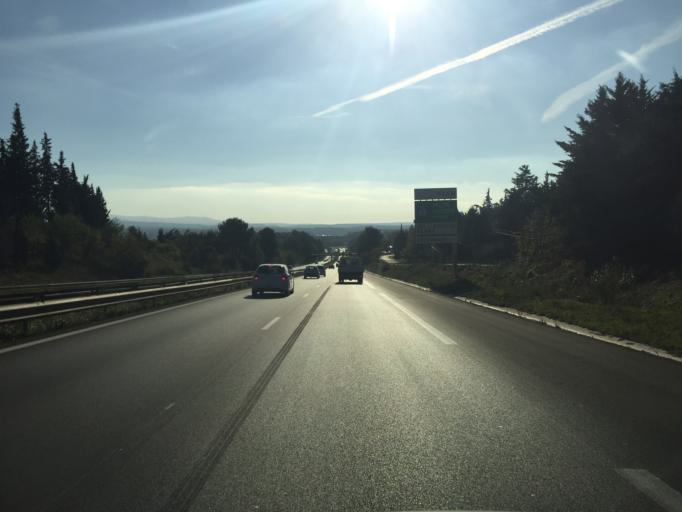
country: FR
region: Provence-Alpes-Cote d'Azur
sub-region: Departement des Bouches-du-Rhone
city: Aix-en-Provence
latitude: 43.5372
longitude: 5.4319
